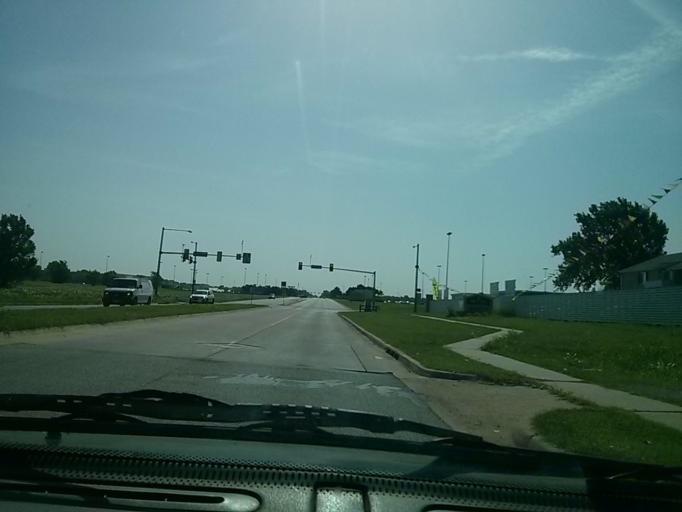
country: US
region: Oklahoma
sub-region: Tulsa County
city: Broken Arrow
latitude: 36.1334
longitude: -95.8245
